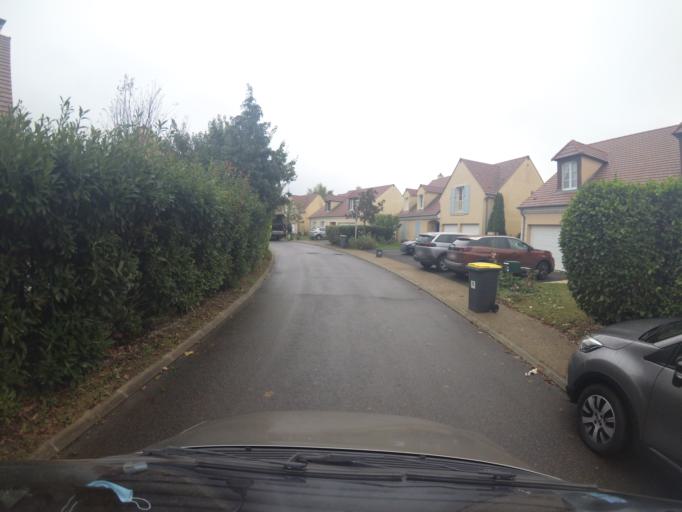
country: FR
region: Ile-de-France
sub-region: Departement de Seine-et-Marne
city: Conches-sur-Gondoire
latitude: 48.8474
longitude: 2.7279
